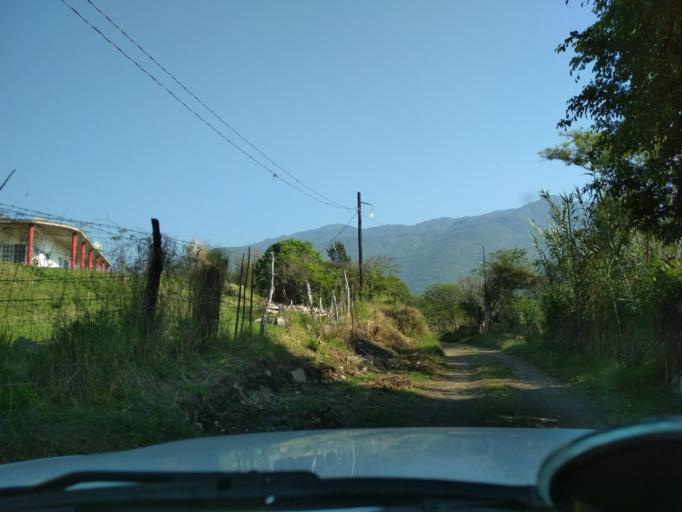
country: MX
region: Veracruz
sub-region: Nogales
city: Agricola Lazaro Cardenas
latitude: 18.8060
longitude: -97.2008
